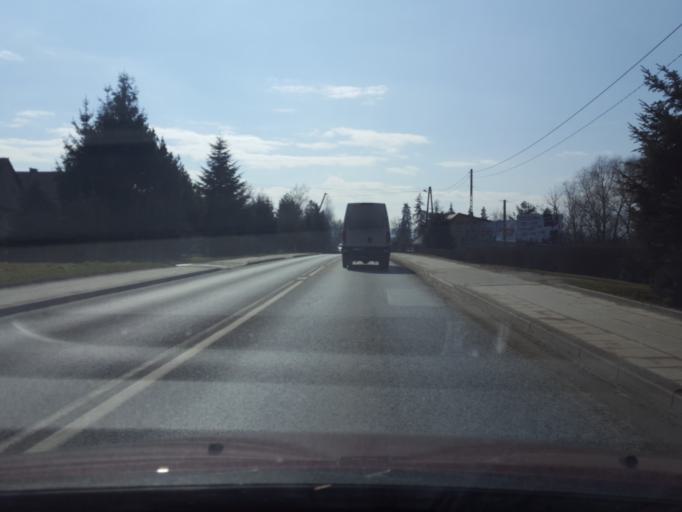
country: PL
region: Lesser Poland Voivodeship
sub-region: Powiat nowosadecki
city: Chelmiec
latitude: 49.6677
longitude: 20.6875
